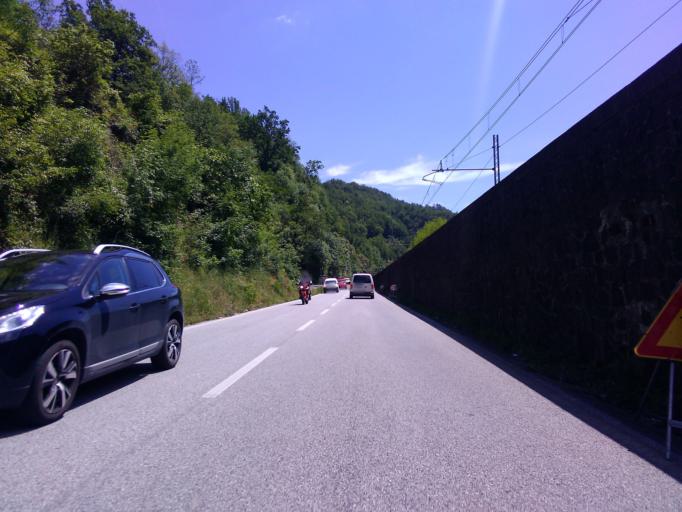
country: IT
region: Tuscany
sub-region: Provincia di Massa-Carrara
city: Villafranca in Lunigiana
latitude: 44.2772
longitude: 9.9530
